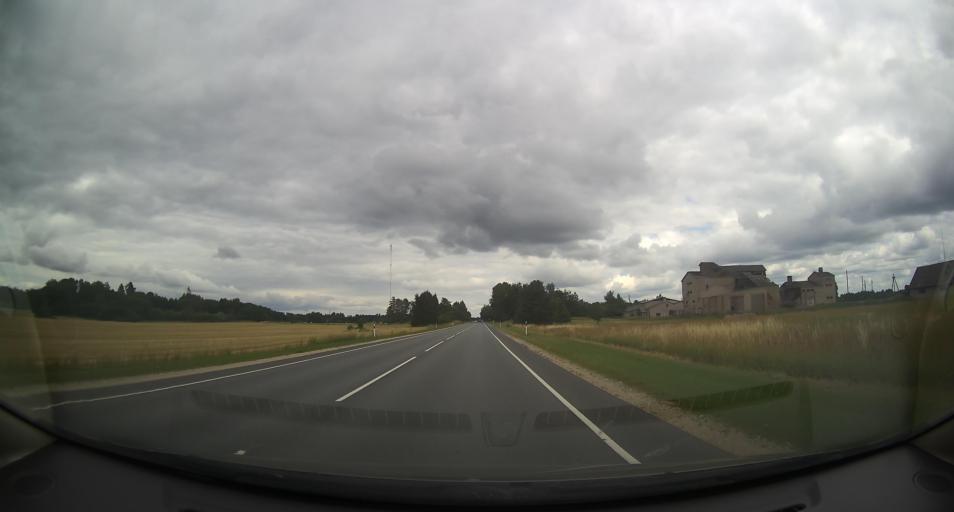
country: EE
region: Harju
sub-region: Nissi vald
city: Turba
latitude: 59.0399
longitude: 24.1661
